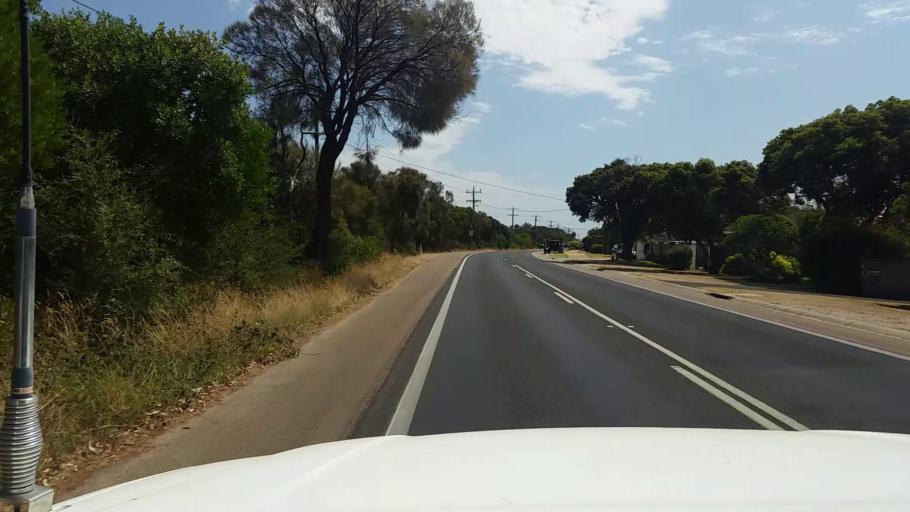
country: AU
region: Victoria
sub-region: Mornington Peninsula
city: Mornington
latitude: -38.2376
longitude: 145.0290
